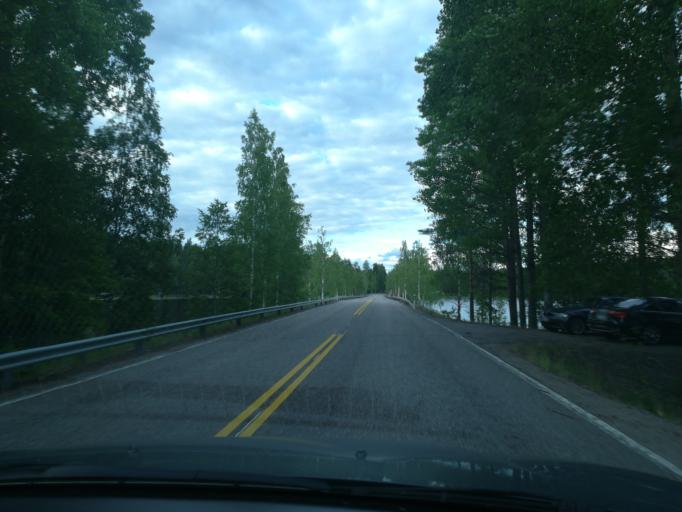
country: FI
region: Southern Savonia
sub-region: Mikkeli
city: Puumala
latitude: 61.5613
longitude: 27.9864
